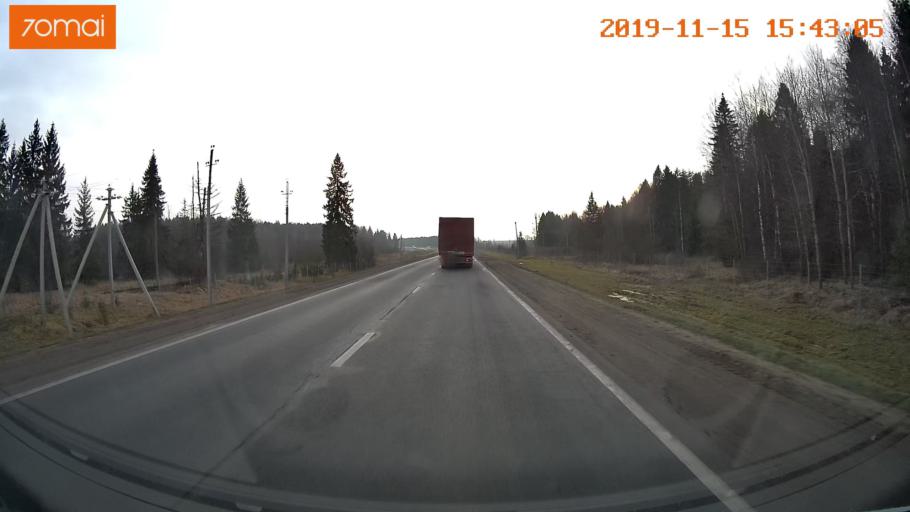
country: RU
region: Jaroslavl
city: Danilov
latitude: 57.9863
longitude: 40.0318
